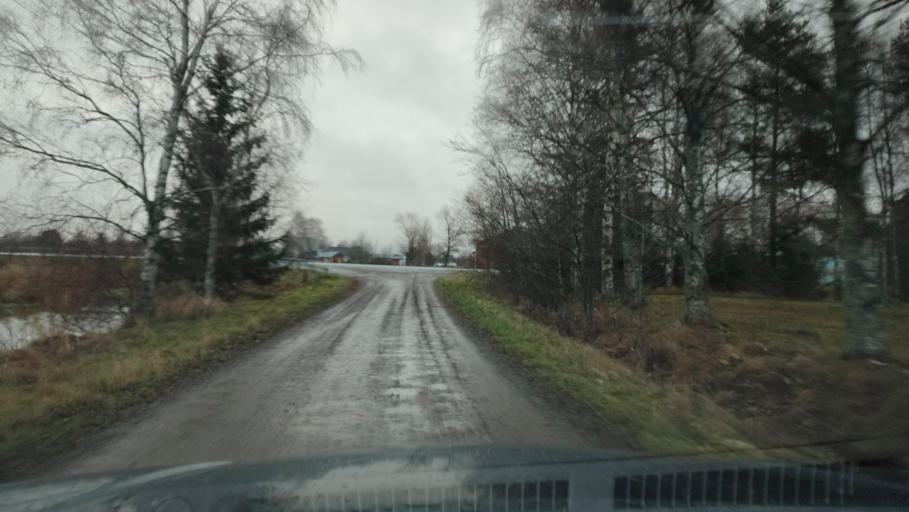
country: FI
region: Ostrobothnia
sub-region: Sydosterbotten
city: Kristinestad
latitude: 62.2449
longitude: 21.5000
